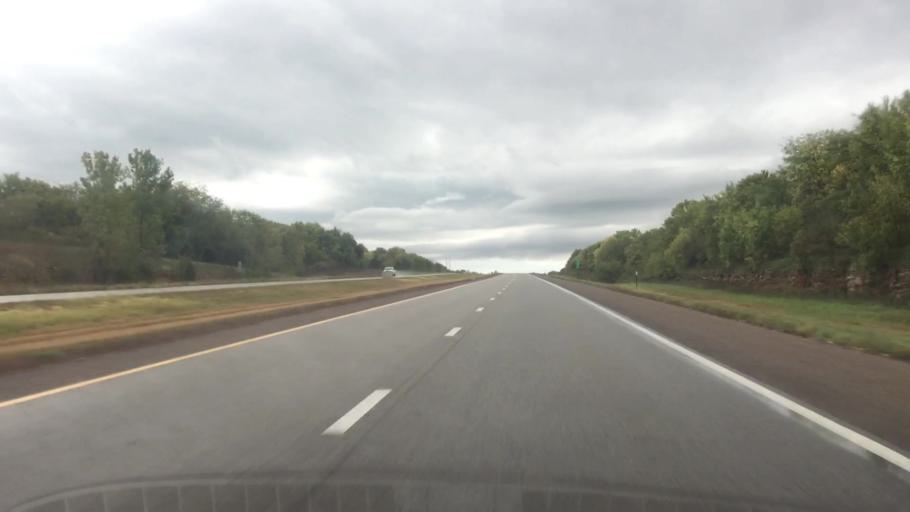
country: US
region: Kansas
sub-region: Miami County
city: Paola
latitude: 38.5953
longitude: -94.8356
